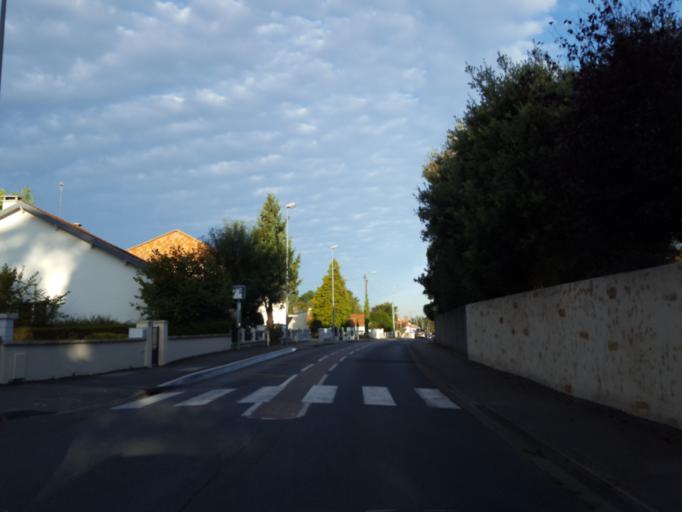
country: FR
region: Pays de la Loire
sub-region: Departement de la Loire-Atlantique
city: Basse-Goulaine
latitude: 47.1920
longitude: -1.4757
